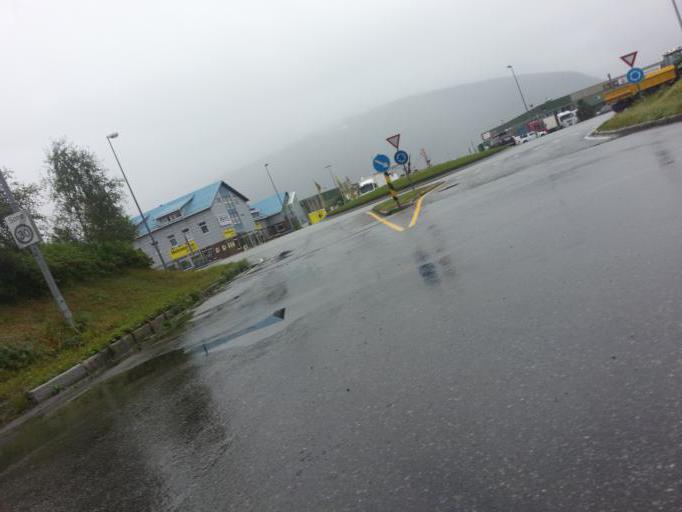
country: NO
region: Troms
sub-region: Tromso
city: Tromso
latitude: 69.6783
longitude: 18.9799
